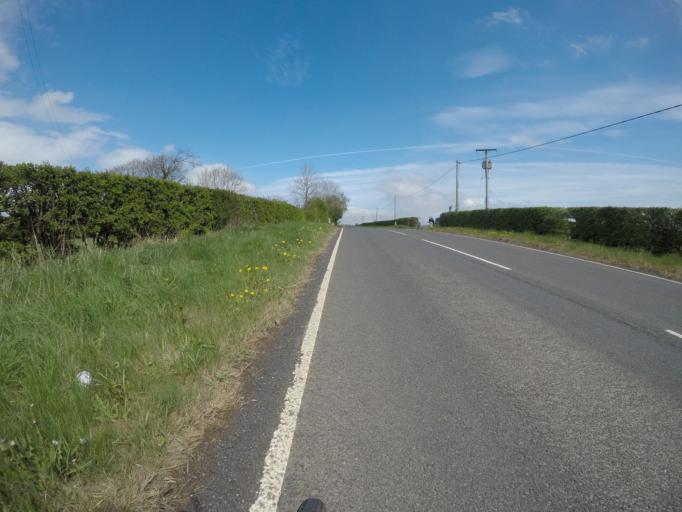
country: GB
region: Scotland
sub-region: East Ayrshire
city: Kilmaurs
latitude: 55.6614
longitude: -4.5484
